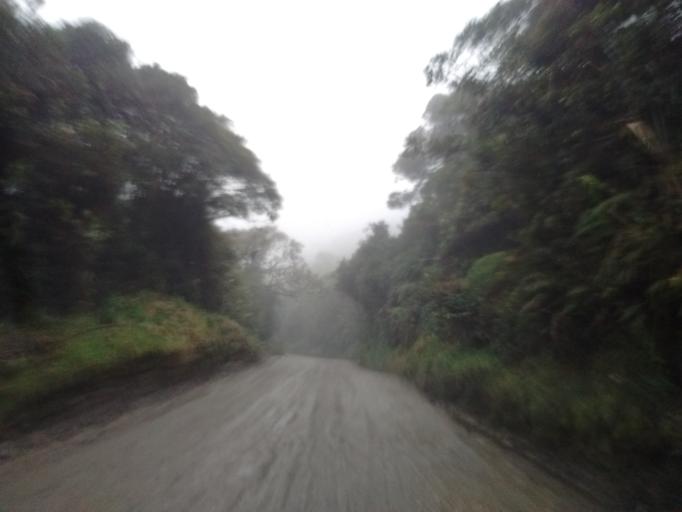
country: CO
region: Cauca
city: Paispamba
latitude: 2.1493
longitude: -76.4467
